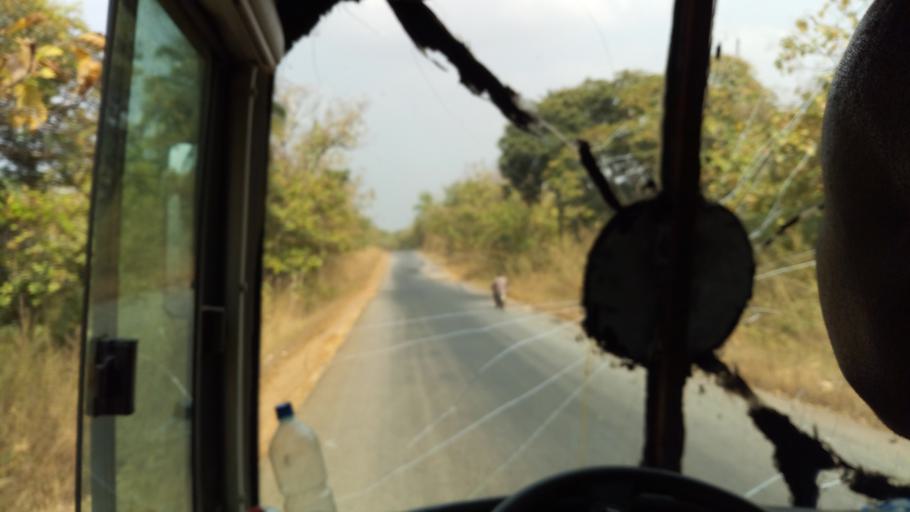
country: TG
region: Centrale
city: Sokode
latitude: 9.1624
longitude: 1.1731
